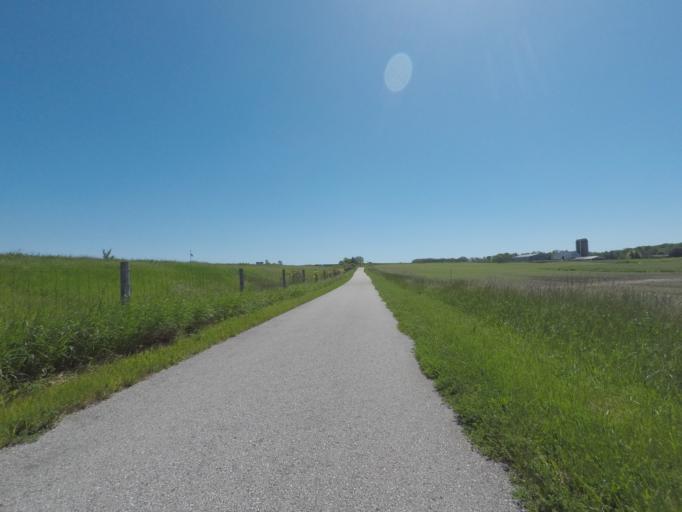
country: US
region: Wisconsin
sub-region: Sheboygan County
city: Sheboygan Falls
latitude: 43.7501
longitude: -87.8057
